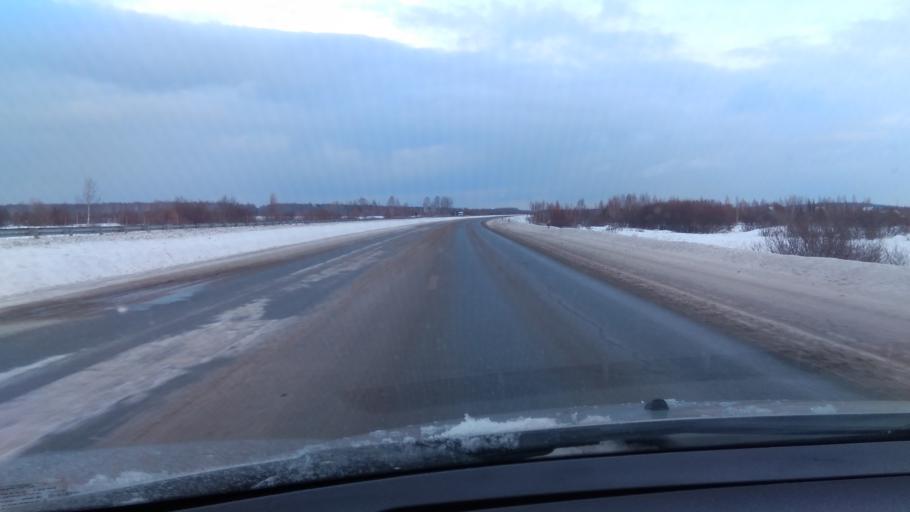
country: RU
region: Sverdlovsk
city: Nev'yansk
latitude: 57.5133
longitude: 60.1768
